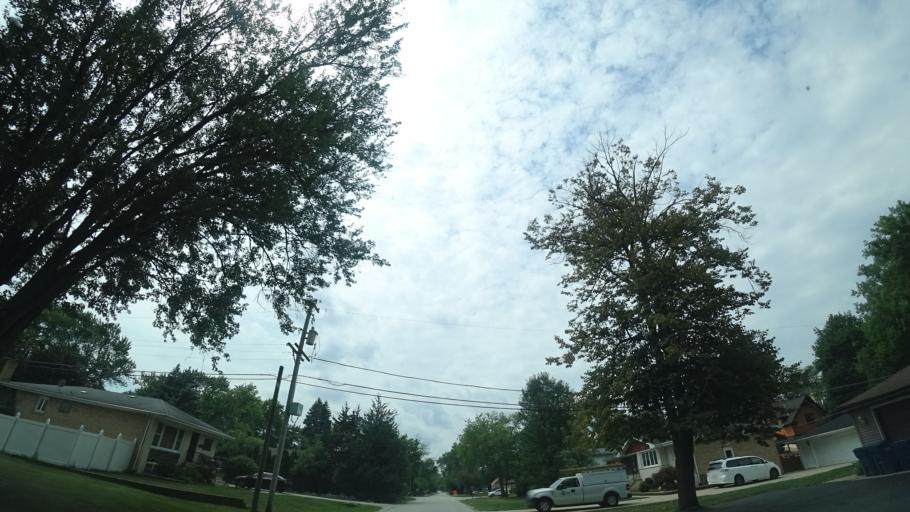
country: US
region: Illinois
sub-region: Cook County
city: Worth
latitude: 41.6846
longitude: -87.7873
